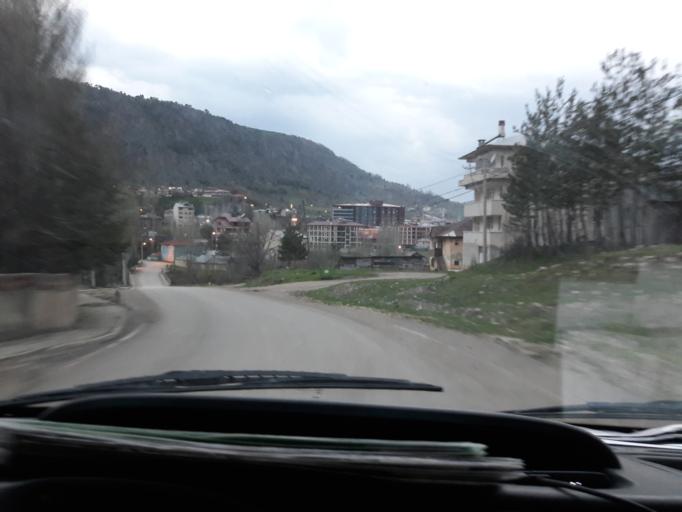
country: TR
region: Giresun
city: Alucra
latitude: 40.3232
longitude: 38.7676
